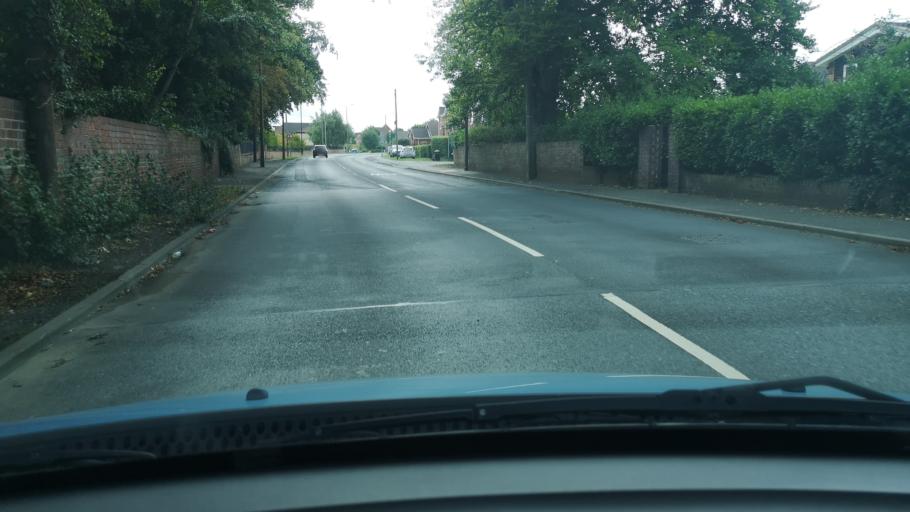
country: GB
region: England
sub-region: Doncaster
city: Hatfield
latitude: 53.5740
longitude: -1.0070
